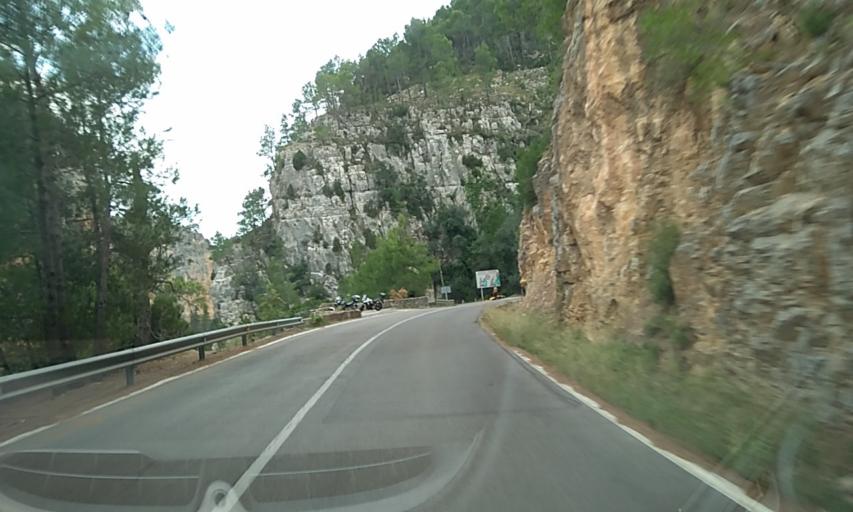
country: ES
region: Valencia
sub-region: Provincia de Castello
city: Montanejos
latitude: 40.0825
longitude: -0.5404
